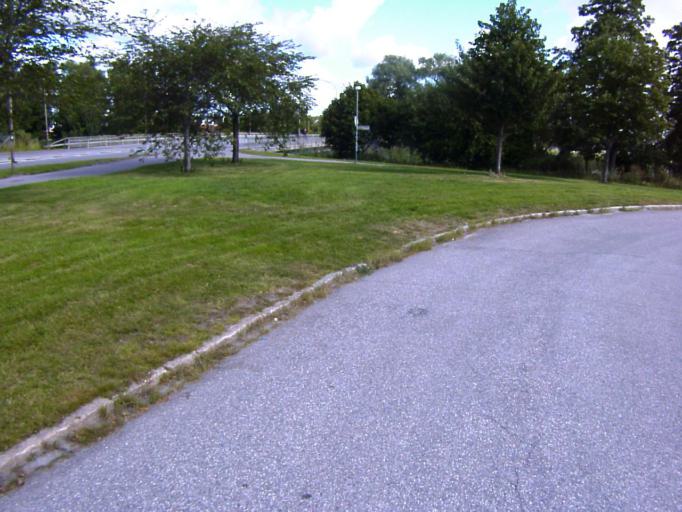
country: SE
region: Soedermanland
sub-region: Eskilstuna Kommun
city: Eskilstuna
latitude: 59.3804
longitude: 16.4985
